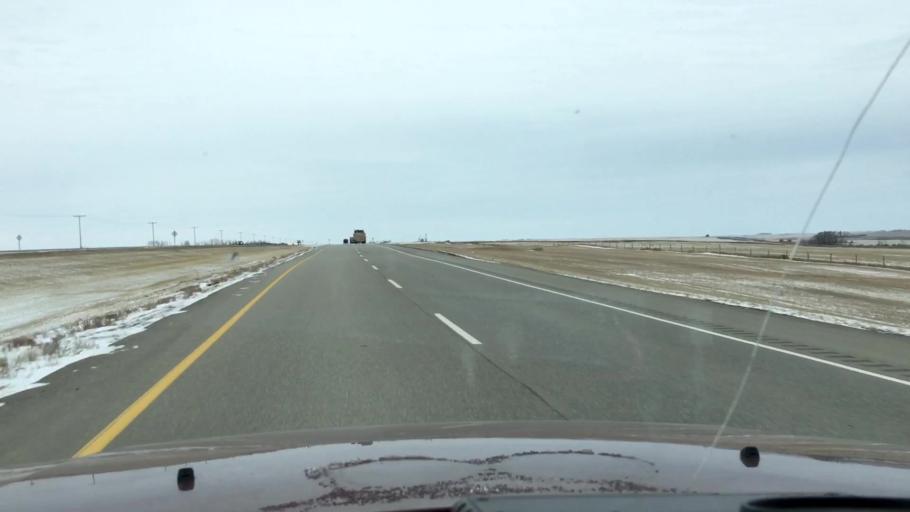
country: CA
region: Saskatchewan
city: Watrous
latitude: 51.2315
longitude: -105.9617
